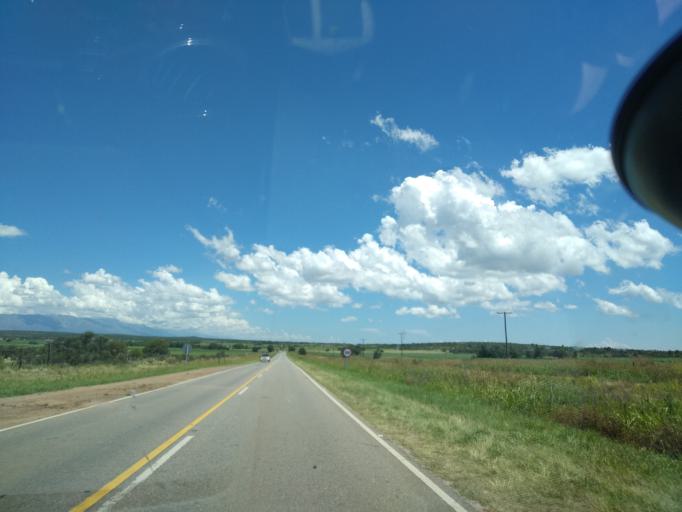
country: AR
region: Cordoba
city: Villa Cura Brochero
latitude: -31.6587
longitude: -65.0987
